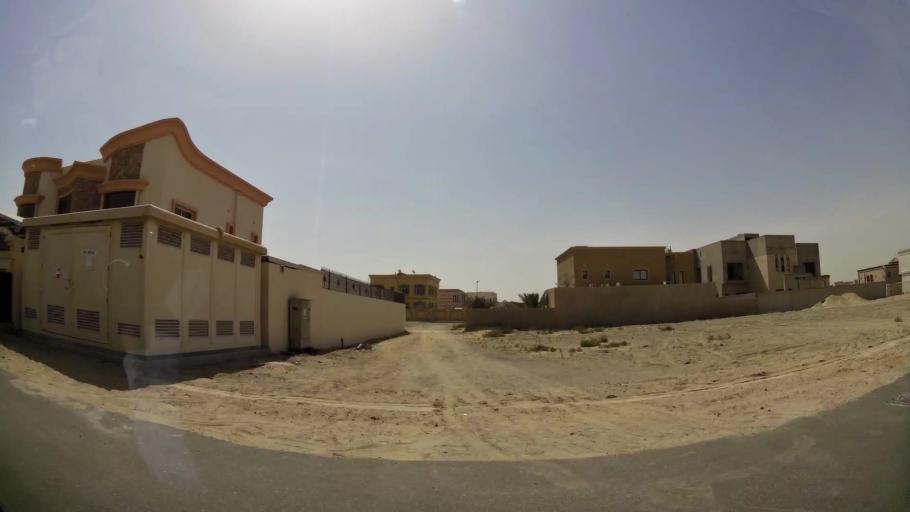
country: AE
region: Ash Shariqah
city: Sharjah
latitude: 25.2048
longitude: 55.4227
